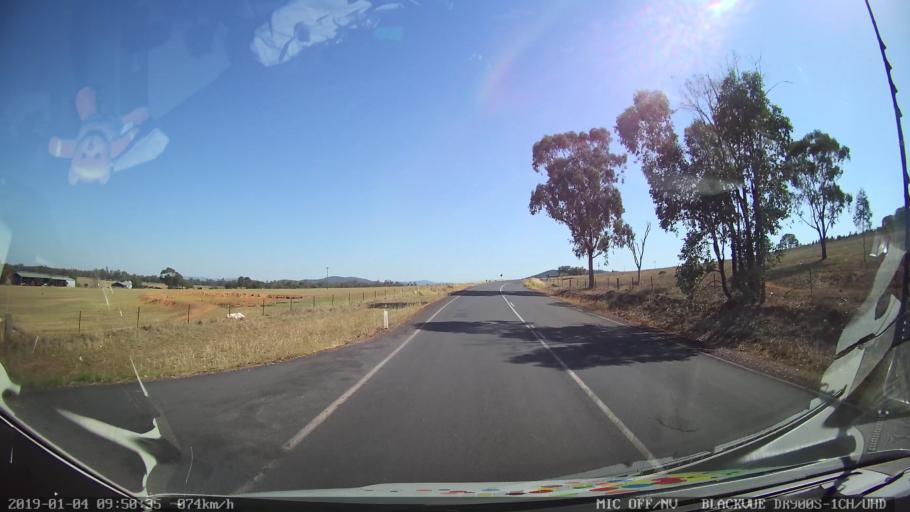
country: AU
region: New South Wales
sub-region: Cabonne
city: Canowindra
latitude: -33.5826
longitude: 148.4159
